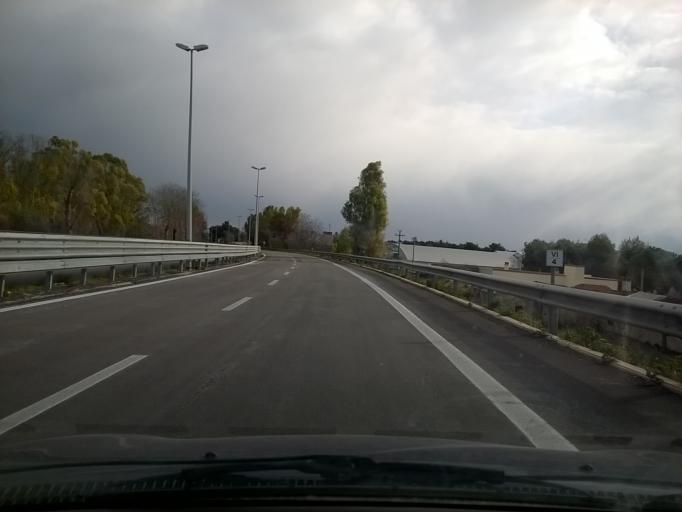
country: IT
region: Apulia
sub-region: Provincia di Taranto
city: Paolo VI
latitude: 40.4674
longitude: 17.2786
